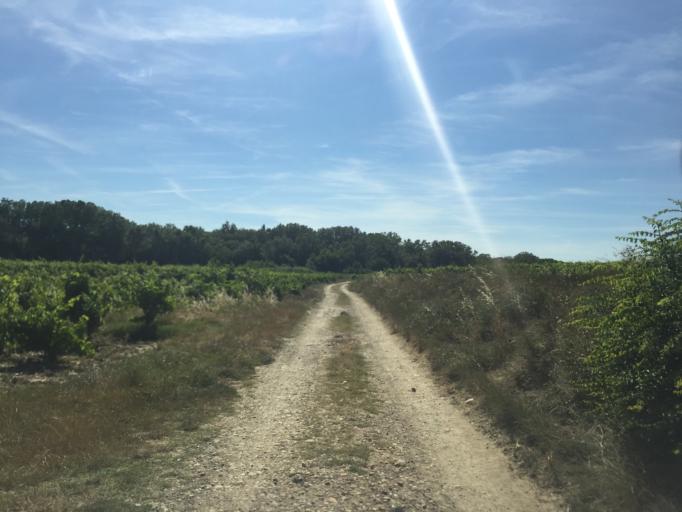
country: FR
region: Provence-Alpes-Cote d'Azur
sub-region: Departement du Vaucluse
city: Chateauneuf-du-Pape
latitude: 44.0472
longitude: 4.8189
